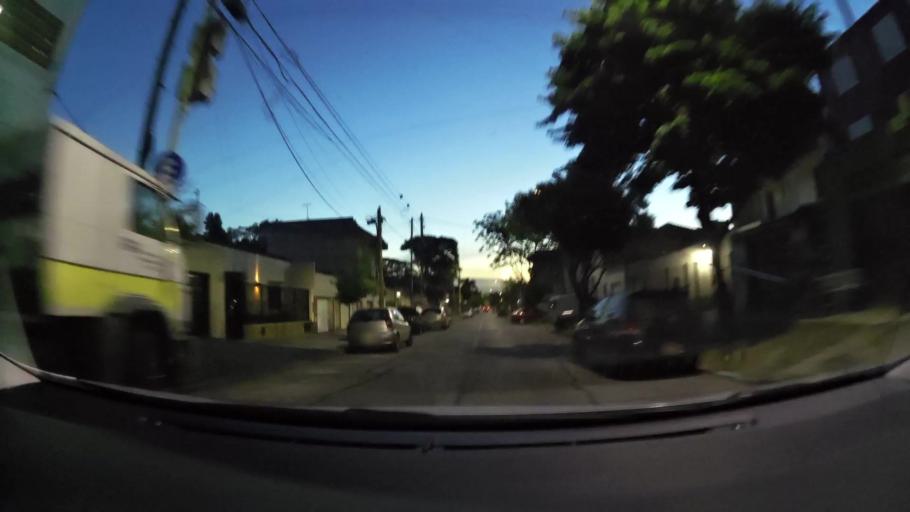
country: AR
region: Buenos Aires F.D.
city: Villa Lugano
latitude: -34.6852
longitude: -58.4792
